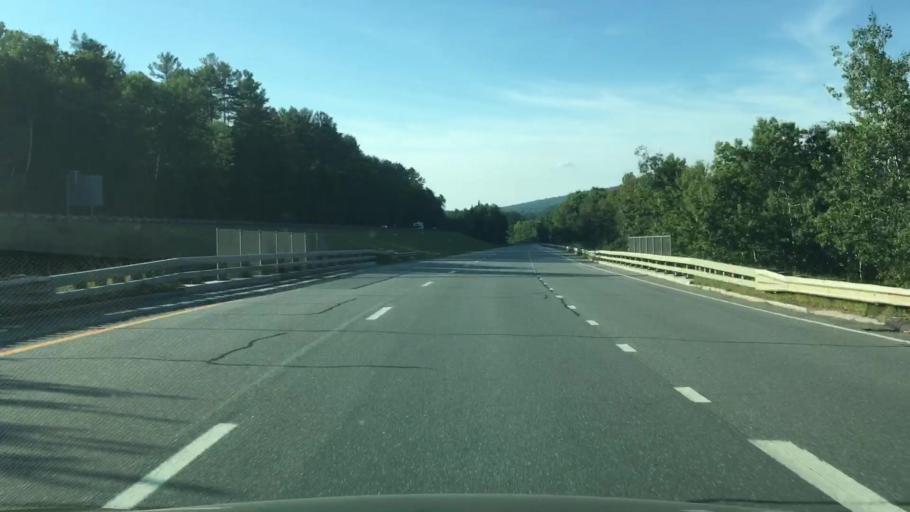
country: US
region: New Hampshire
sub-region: Grafton County
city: Littleton
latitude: 44.2975
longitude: -71.7718
